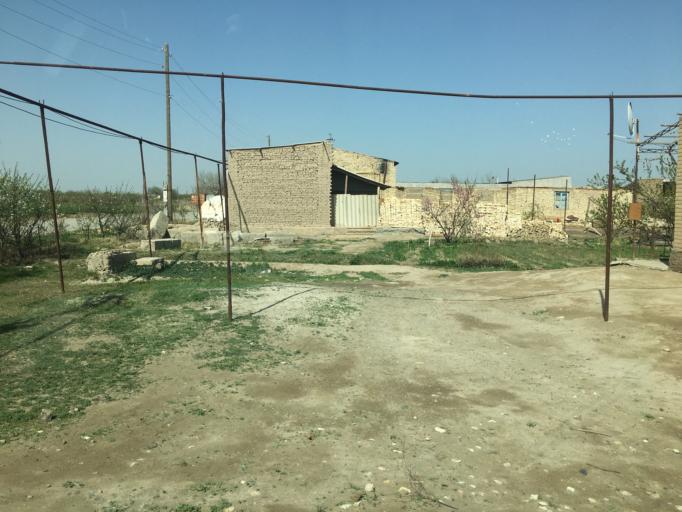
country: TM
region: Lebap
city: Turkmenabat
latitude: 38.9575
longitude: 63.6471
